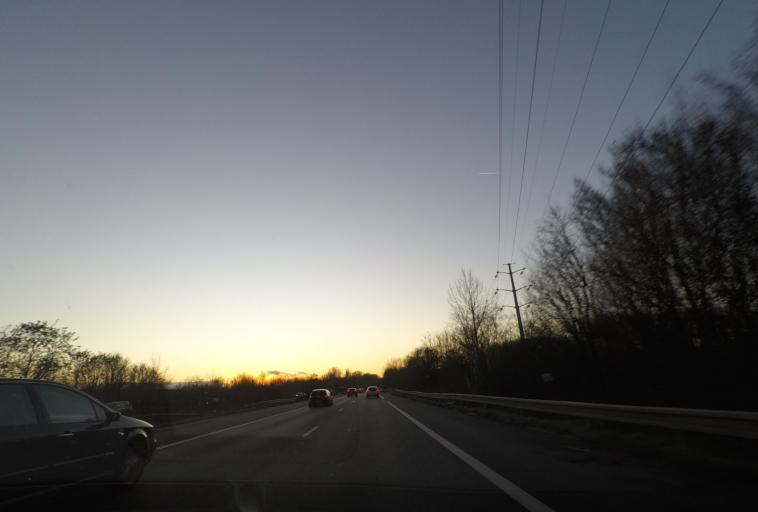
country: FR
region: Ile-de-France
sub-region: Departement de l'Essonne
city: Saint-Michel-sur-Orge
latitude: 48.6243
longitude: 2.2990
